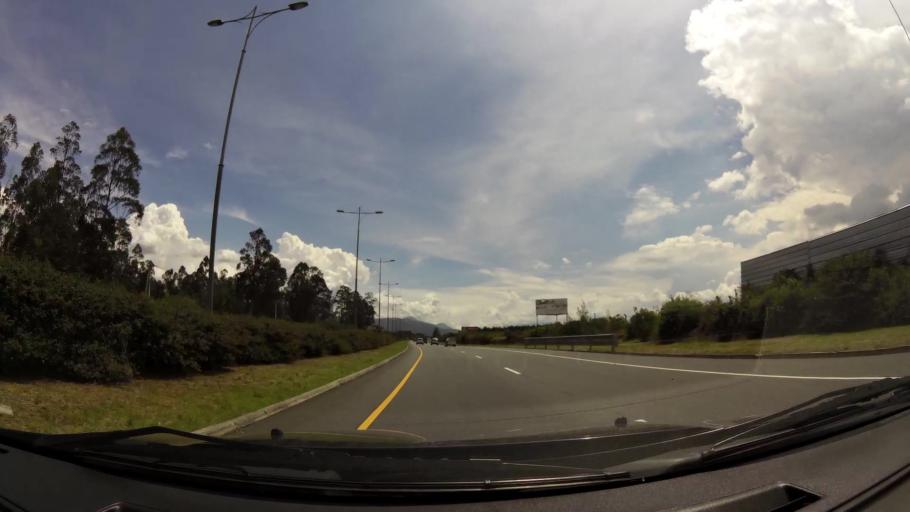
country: EC
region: Pichincha
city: Quito
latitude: -0.1639
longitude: -78.3453
